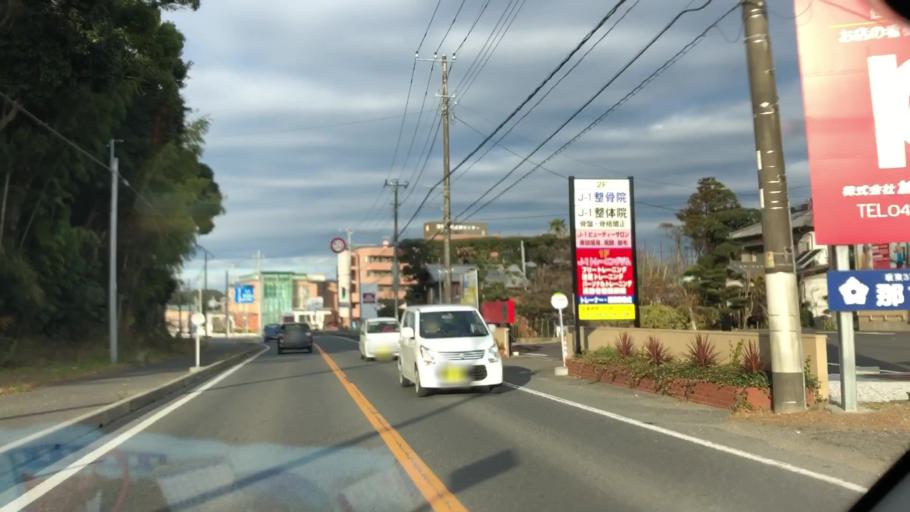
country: JP
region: Chiba
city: Tateyama
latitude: 34.9990
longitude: 139.8940
